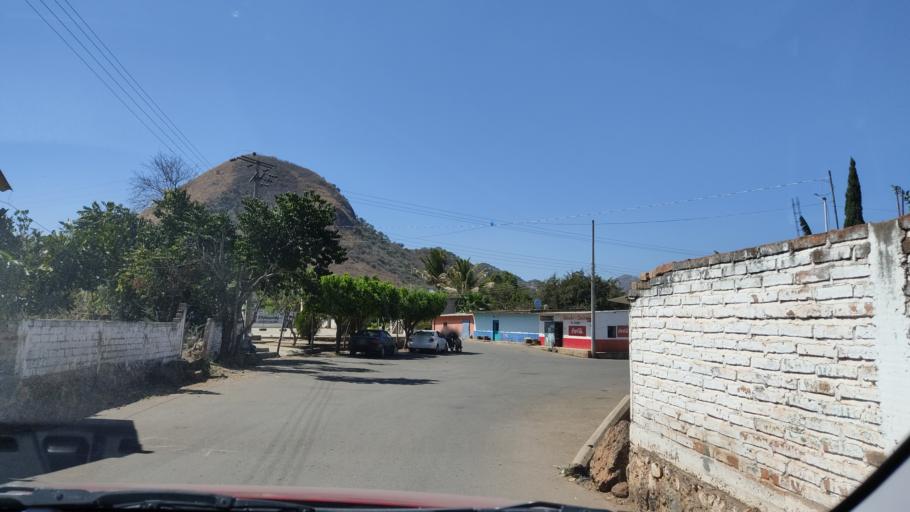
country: MX
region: Nayarit
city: Santa Maria del Oro
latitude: 21.5010
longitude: -104.6226
